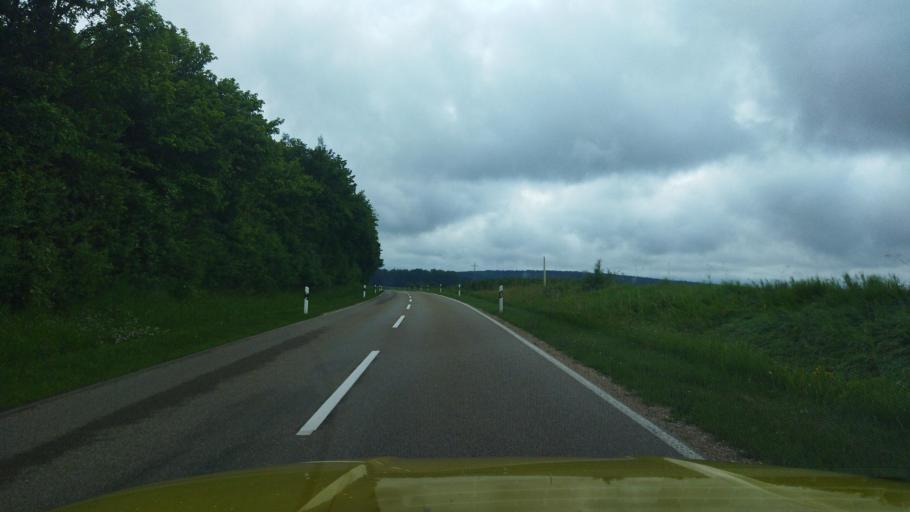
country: DE
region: Bavaria
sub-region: Lower Bavaria
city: Riedenburg
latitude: 48.9526
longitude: 11.6192
